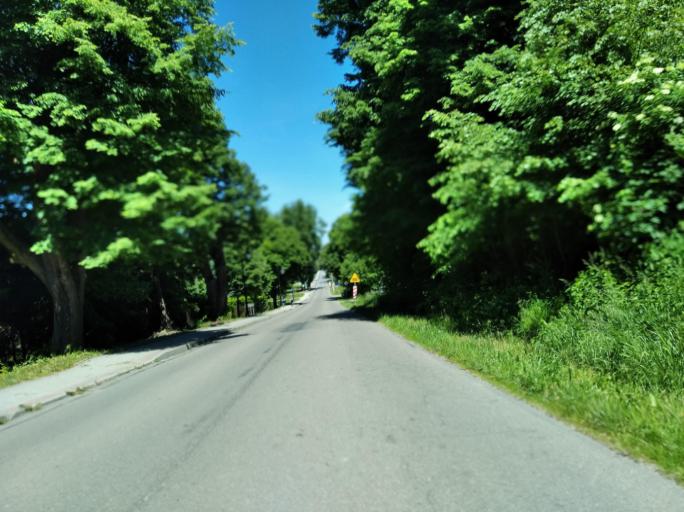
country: PL
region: Subcarpathian Voivodeship
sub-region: Powiat jasielski
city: Tarnowiec
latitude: 49.7347
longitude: 21.5805
